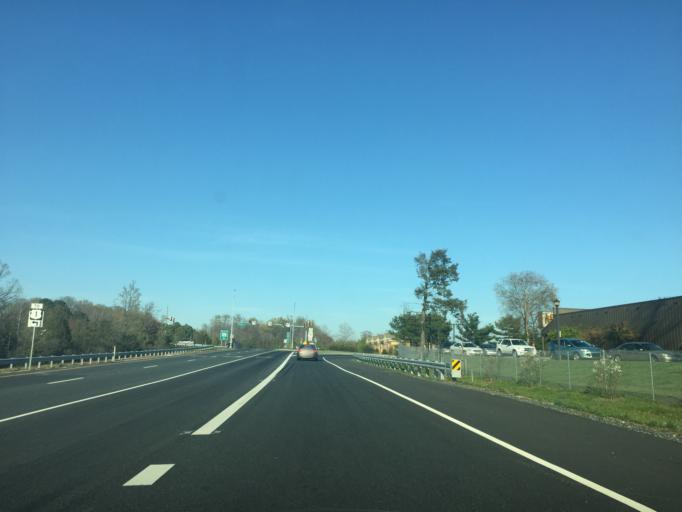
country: US
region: Maryland
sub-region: Harford County
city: Riverside
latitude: 39.4825
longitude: -76.2521
